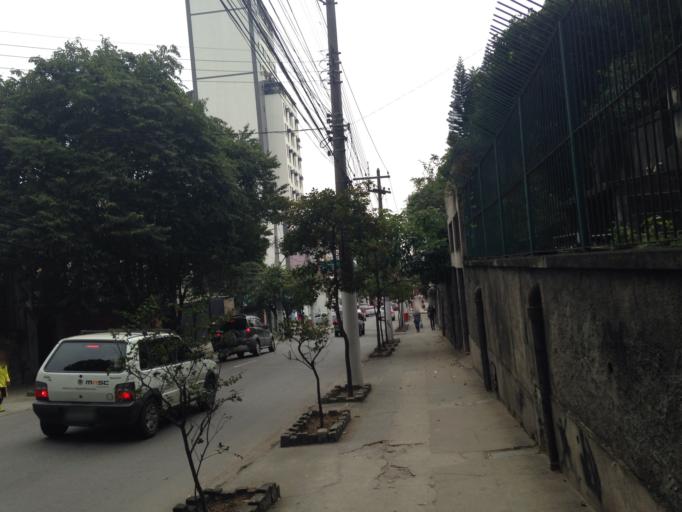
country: BR
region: Rio de Janeiro
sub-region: Niteroi
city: Niteroi
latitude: -22.8995
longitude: -43.1229
